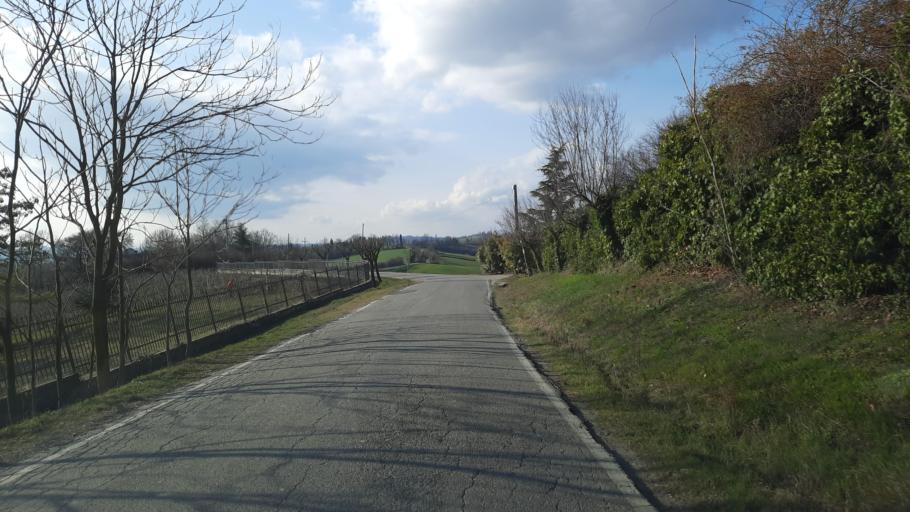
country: IT
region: Piedmont
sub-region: Provincia di Alessandria
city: San Giorgio
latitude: 45.1157
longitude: 8.3968
